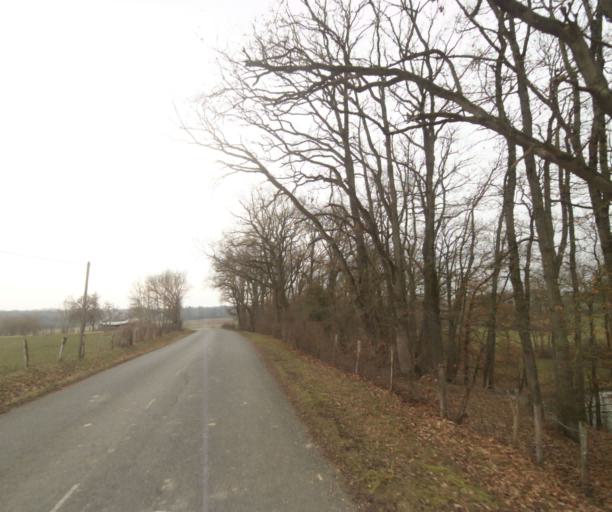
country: FR
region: Champagne-Ardenne
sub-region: Departement de la Marne
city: Pargny-sur-Saulx
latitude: 48.7446
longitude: 4.8420
